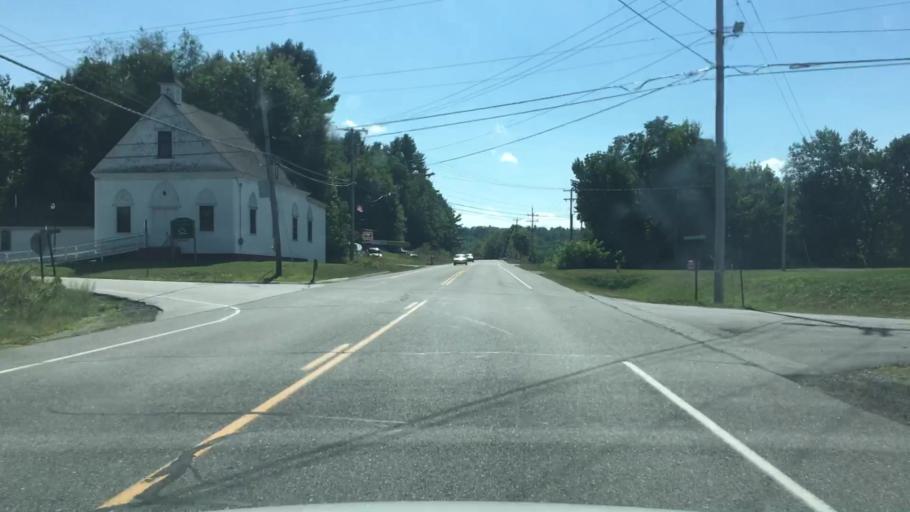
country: US
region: Maine
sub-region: Androscoggin County
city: Greene
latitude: 44.2201
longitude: -70.0918
